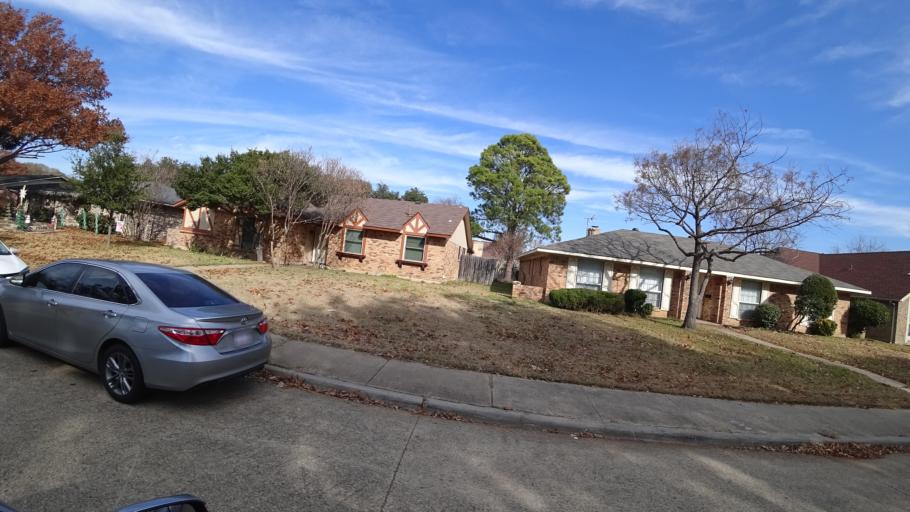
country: US
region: Texas
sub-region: Denton County
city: Lewisville
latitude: 33.0460
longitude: -97.0280
